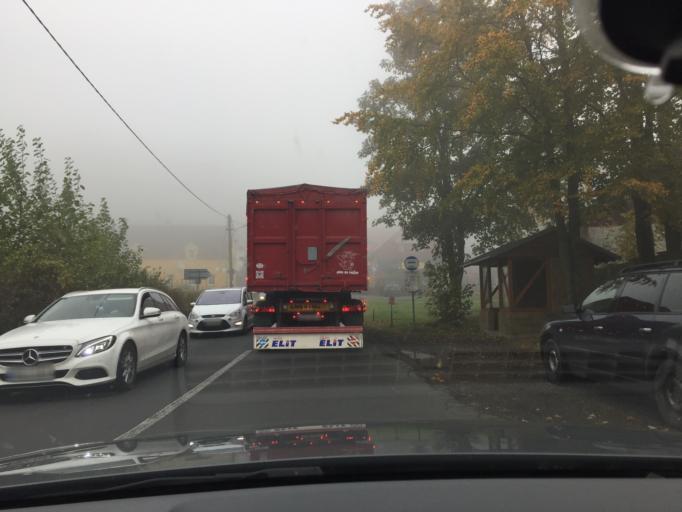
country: CZ
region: Ustecky
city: Libouchec
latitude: 50.7870
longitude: 13.9785
